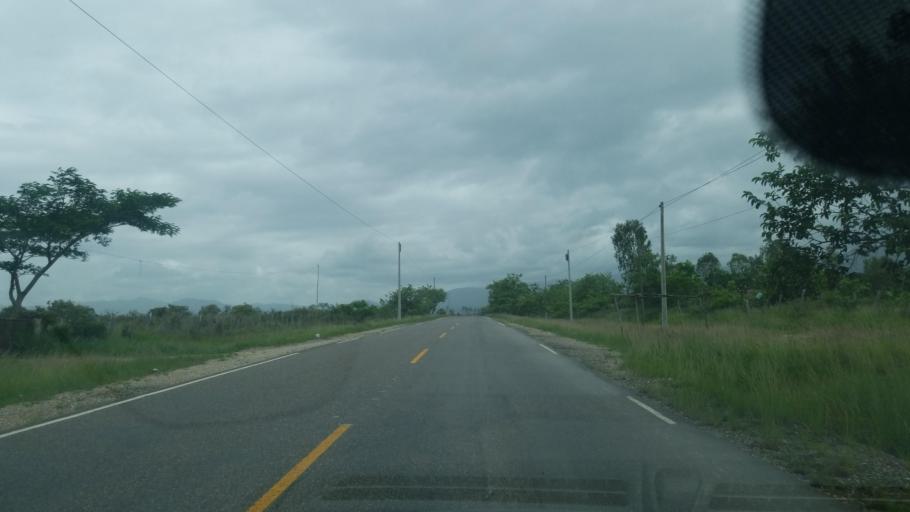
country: HN
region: Ocotepeque
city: Lucerna
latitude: 14.5325
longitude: -88.9500
